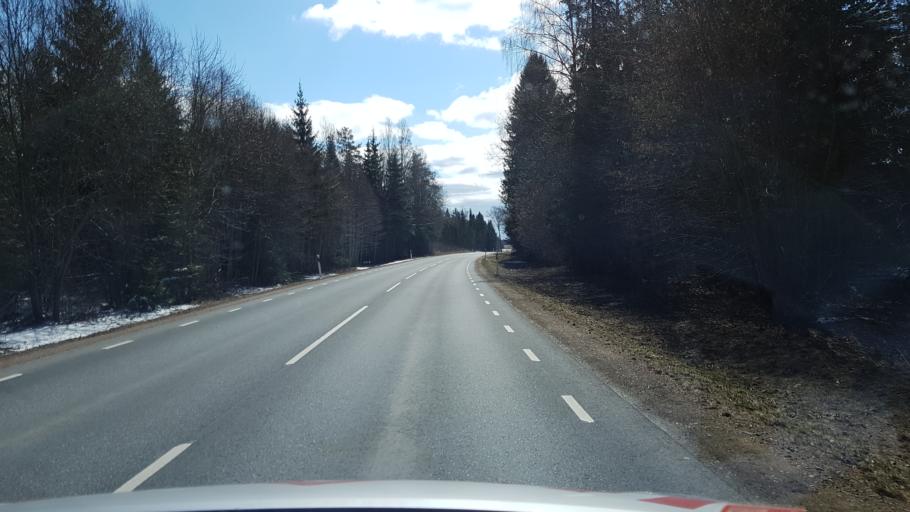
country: EE
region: Laeaene-Virumaa
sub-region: Kadrina vald
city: Kadrina
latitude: 59.3886
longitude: 26.0166
